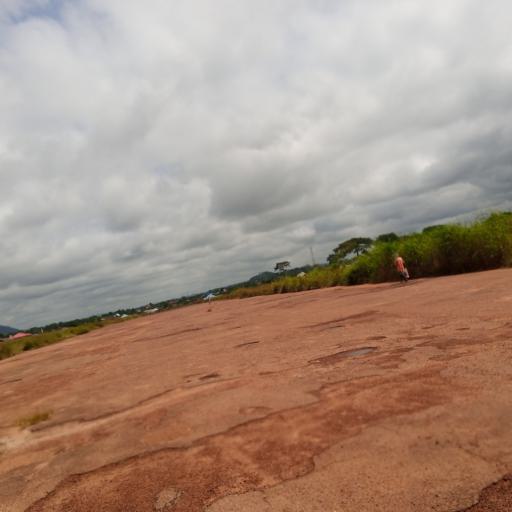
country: SL
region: Eastern Province
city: Kenema
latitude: 7.8969
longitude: -11.1738
